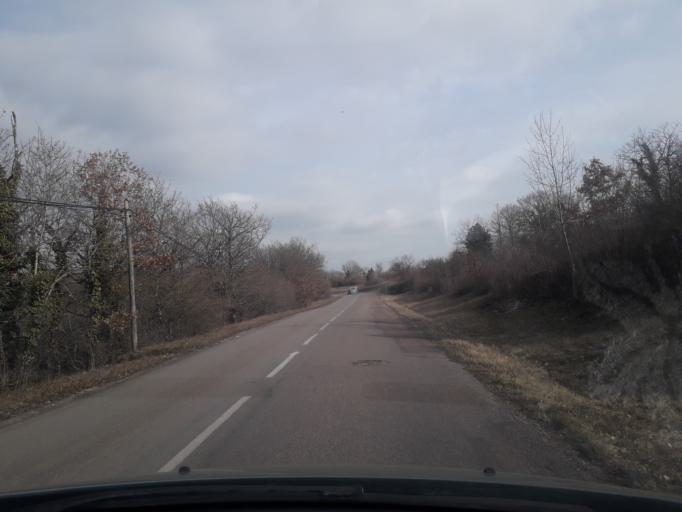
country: FR
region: Bourgogne
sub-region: Departement de la Cote-d'Or
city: Messigny-et-Vantoux
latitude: 47.4124
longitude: 5.0089
